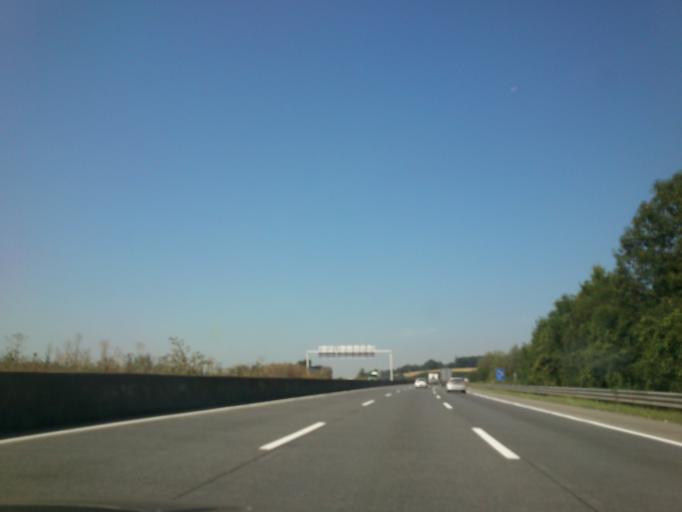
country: AT
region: Upper Austria
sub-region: Politischer Bezirk Linz-Land
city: Traun
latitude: 48.1923
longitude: 14.2346
